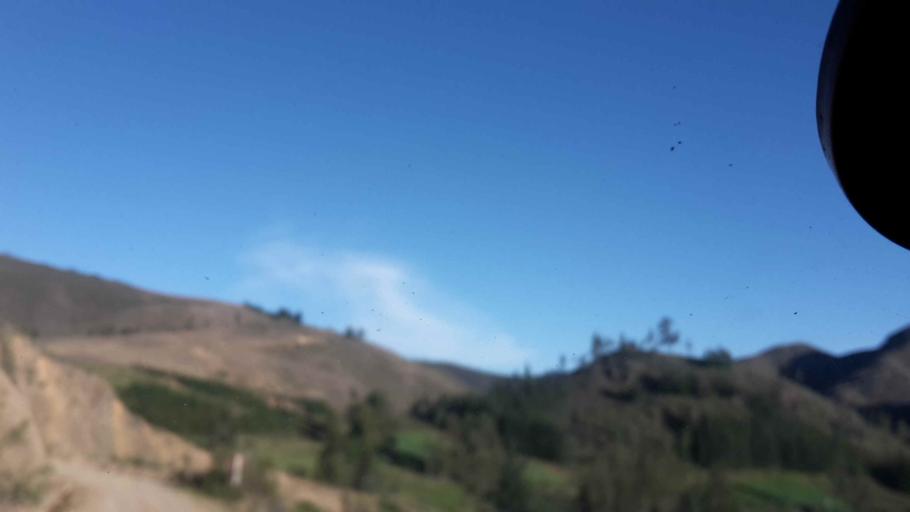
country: BO
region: Cochabamba
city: Arani
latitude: -17.7948
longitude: -65.6005
